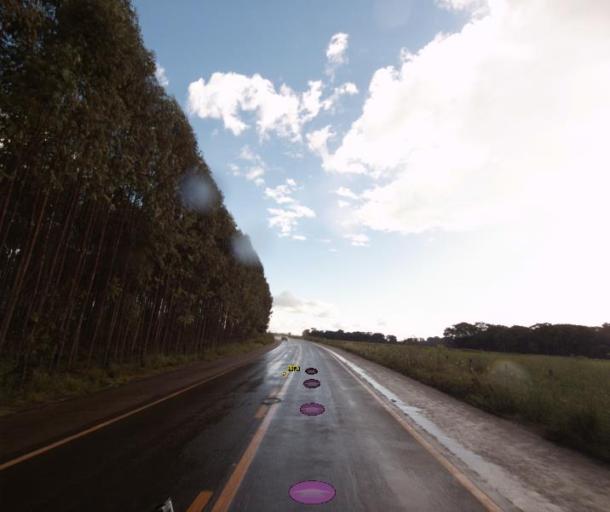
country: BR
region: Goias
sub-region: Itaberai
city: Itaberai
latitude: -16.0131
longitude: -49.7679
